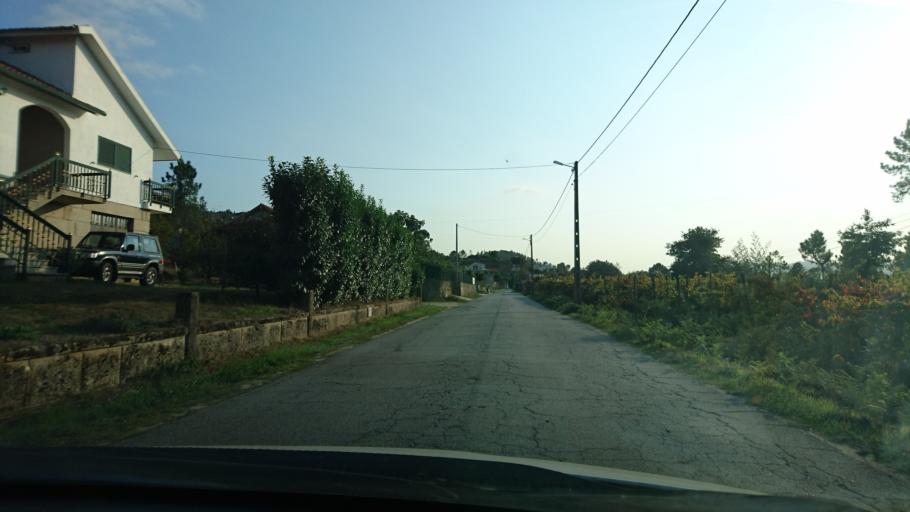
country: PT
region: Vila Real
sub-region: Mondim de Basto
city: Mondim de Basto
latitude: 41.4331
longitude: -7.9286
